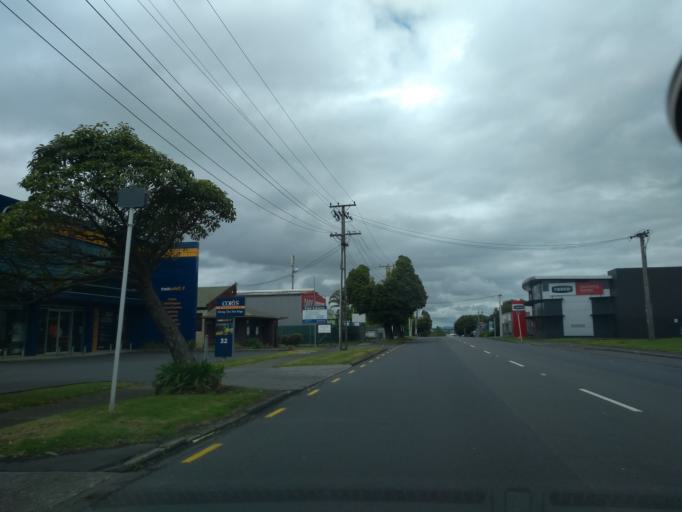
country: NZ
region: Auckland
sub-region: Auckland
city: Tamaki
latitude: -36.9150
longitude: 174.8164
